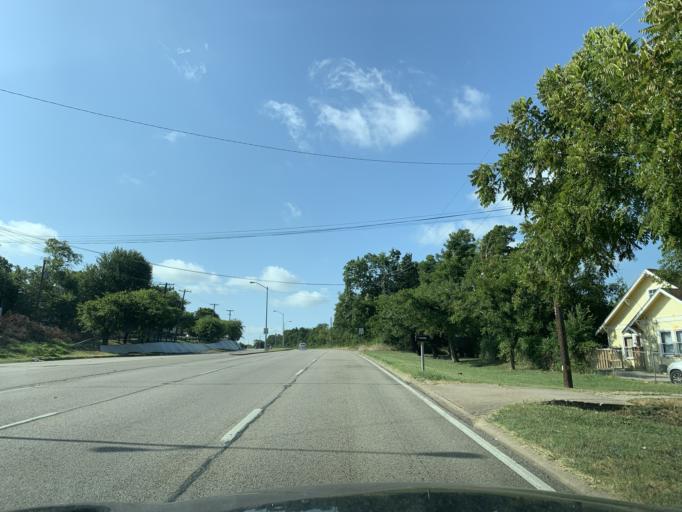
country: US
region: Texas
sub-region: Dallas County
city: Hutchins
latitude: 32.6762
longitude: -96.7852
